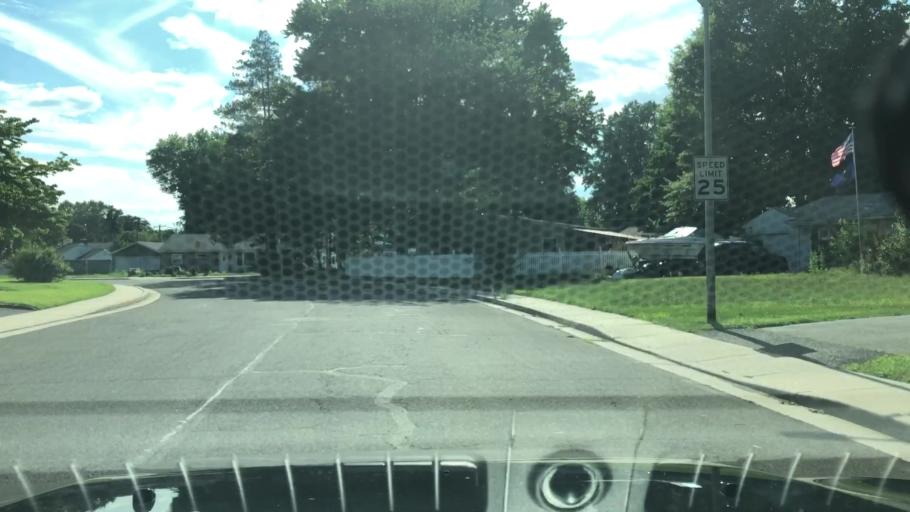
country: US
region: Pennsylvania
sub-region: Bucks County
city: Fairless Hills
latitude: 40.1823
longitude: -74.8527
